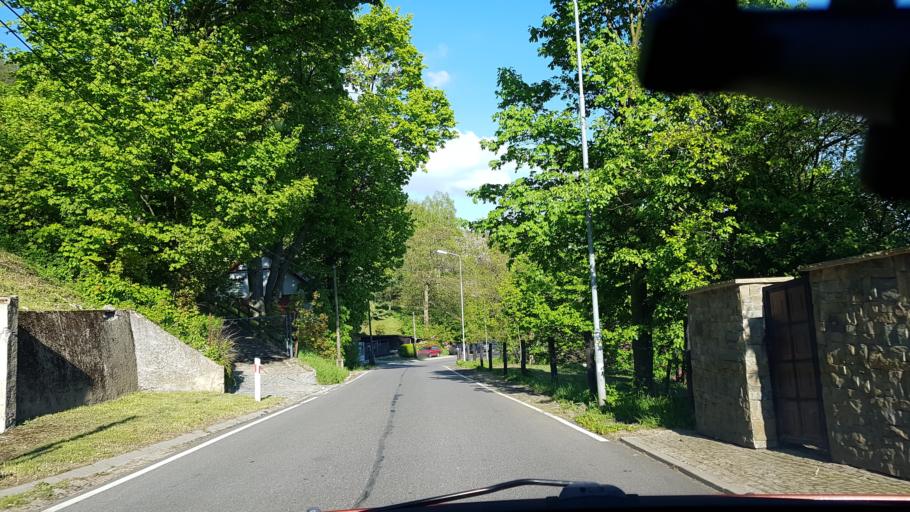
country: PL
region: Lower Silesian Voivodeship
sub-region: Powiat zabkowicki
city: Budzow
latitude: 50.5713
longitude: 16.6398
